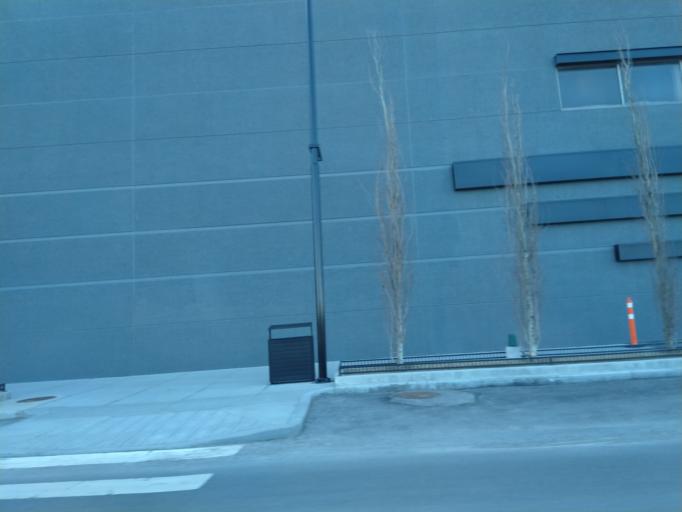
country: CA
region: Alberta
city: Calgary
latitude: 51.1088
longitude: -114.0443
